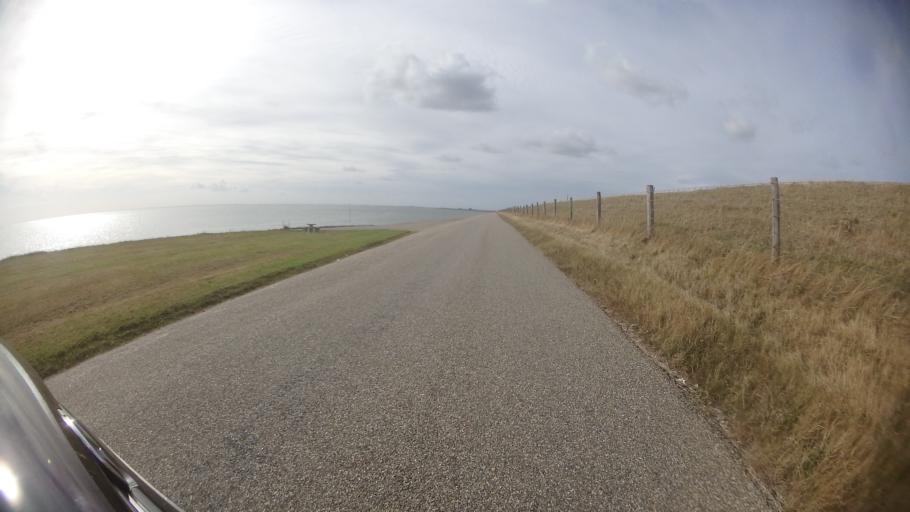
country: NL
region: North Holland
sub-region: Gemeente Texel
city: Den Burg
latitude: 53.0776
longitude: 4.8945
